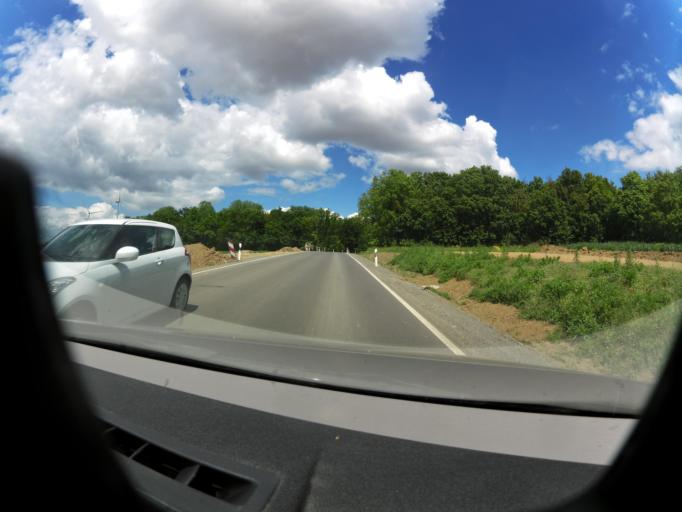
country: DE
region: Bavaria
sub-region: Regierungsbezirk Unterfranken
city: Schwanfeld
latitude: 49.9329
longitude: 10.1370
